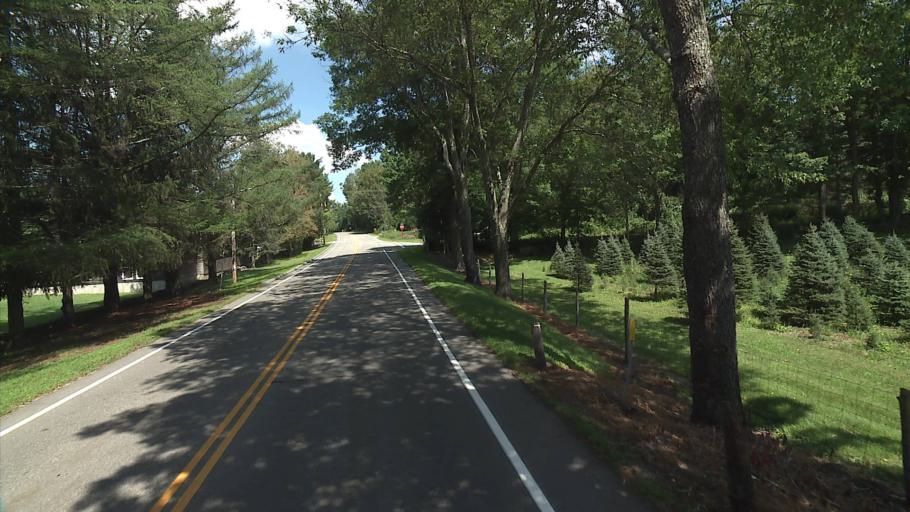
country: US
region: Connecticut
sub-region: Windham County
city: South Woodstock
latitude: 41.9417
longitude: -72.0739
